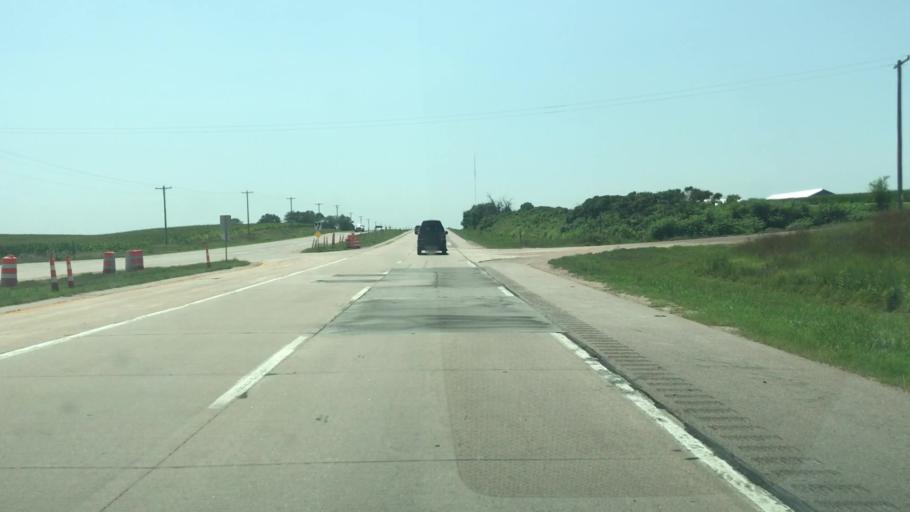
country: US
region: Nebraska
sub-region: Adams County
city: Hastings
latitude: 40.6703
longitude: -98.3823
